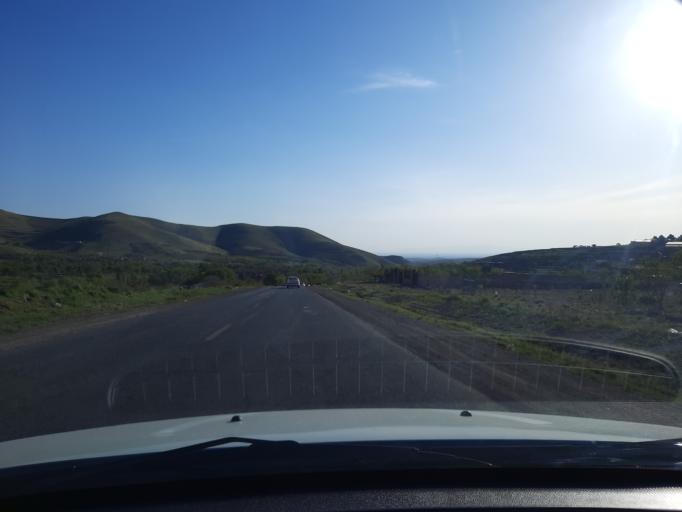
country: IR
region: Qazvin
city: Qazvin
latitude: 36.3475
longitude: 50.1845
